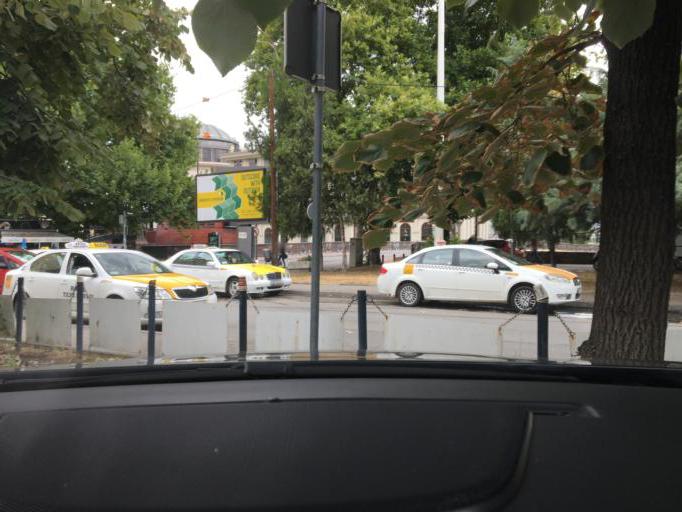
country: MK
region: Karpos
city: Skopje
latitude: 41.9947
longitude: 21.4371
